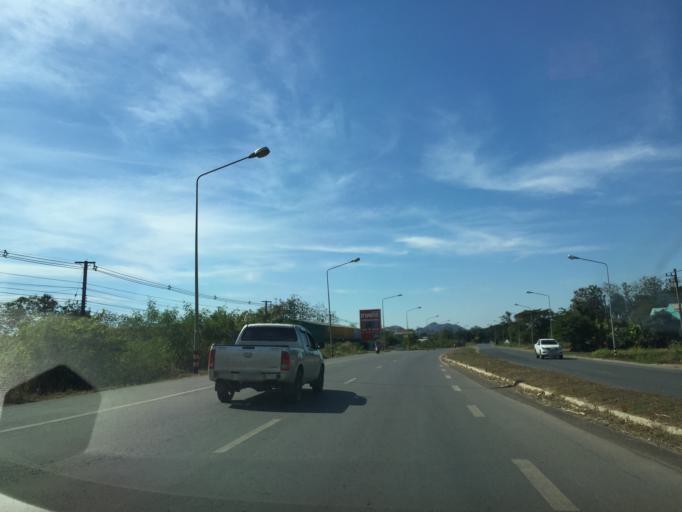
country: TH
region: Changwat Nong Bua Lamphu
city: Na Wang
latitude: 17.3202
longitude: 102.1027
